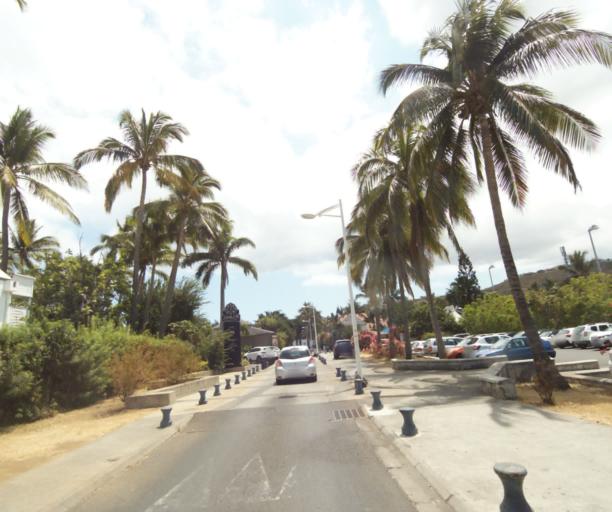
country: RE
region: Reunion
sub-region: Reunion
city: Saint-Paul
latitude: -21.0714
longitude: 55.2236
